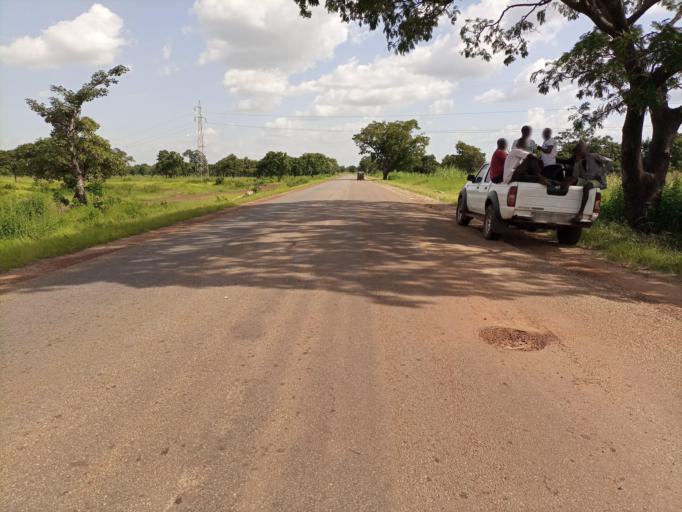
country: GH
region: Northern
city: Savelugu
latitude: 9.5691
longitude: -0.9890
